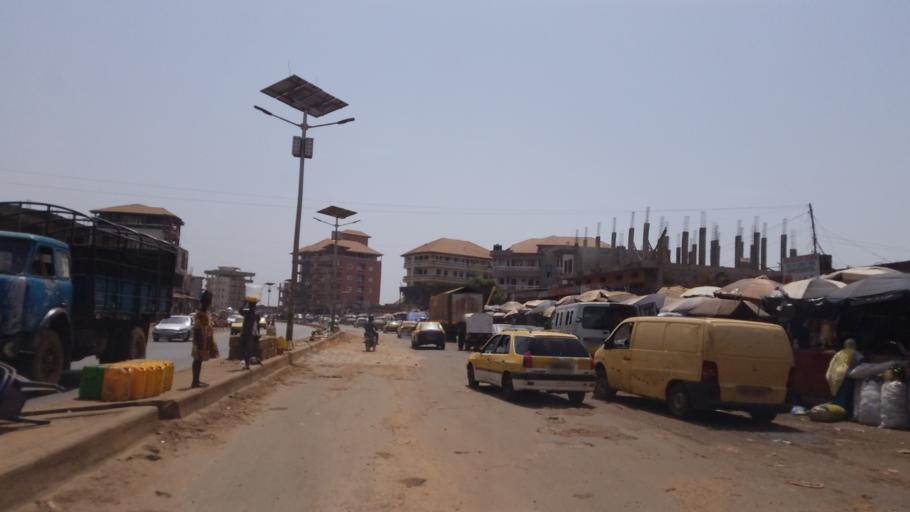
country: GN
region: Kindia
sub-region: Prefecture de Dubreka
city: Dubreka
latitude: 9.6658
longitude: -13.5617
